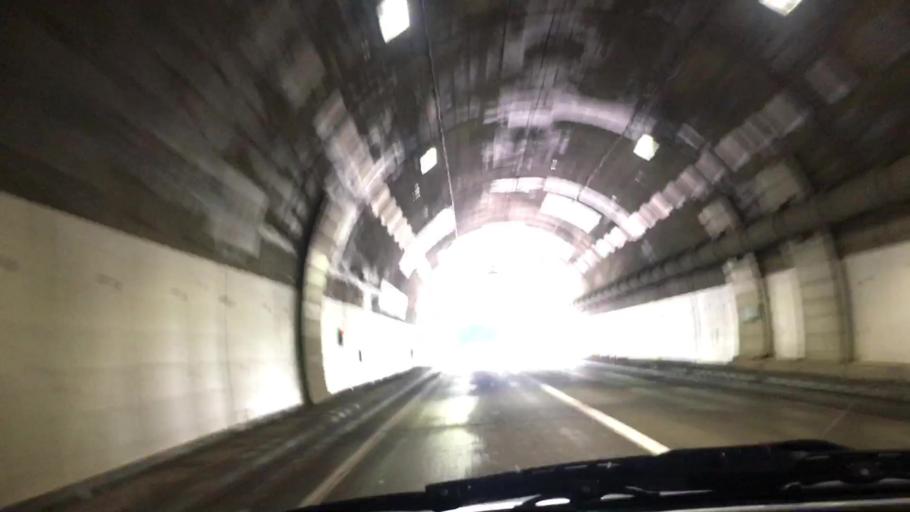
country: JP
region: Hokkaido
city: Otofuke
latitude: 43.3673
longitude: 143.2053
